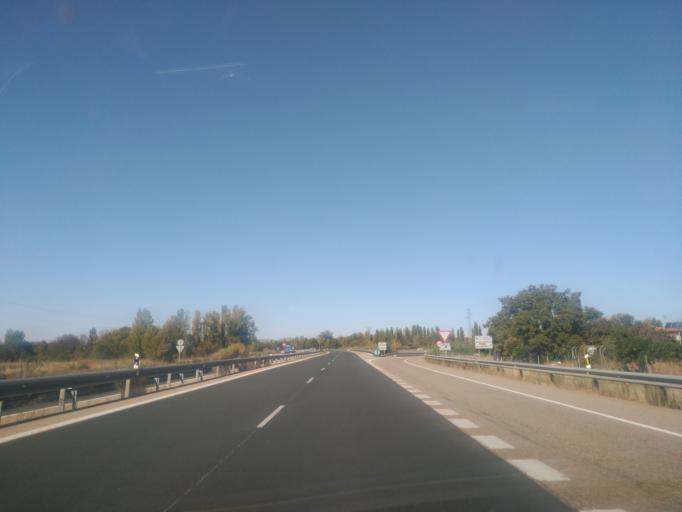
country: ES
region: Castille and Leon
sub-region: Provincia de Valladolid
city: Tudela de Duero
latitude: 41.5931
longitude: -4.5752
